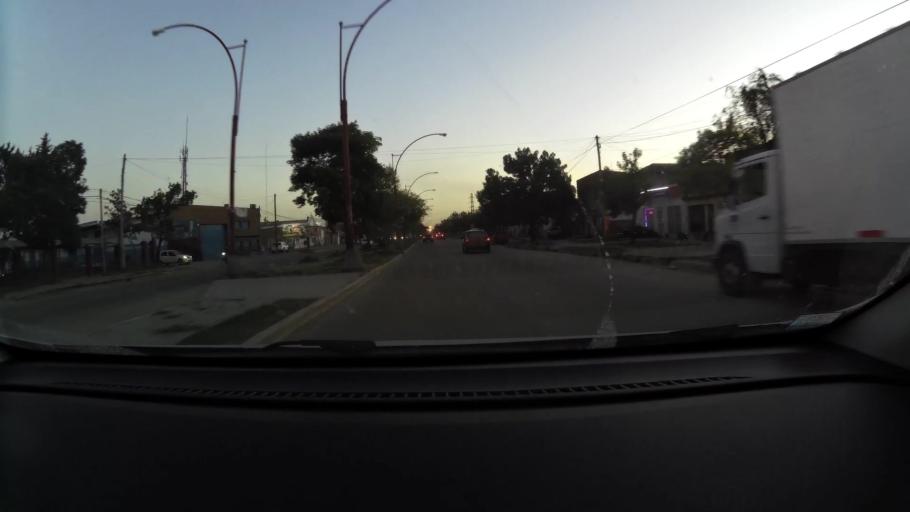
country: AR
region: Santa Fe
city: Santa Fe de la Vera Cruz
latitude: -31.6056
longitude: -60.7131
